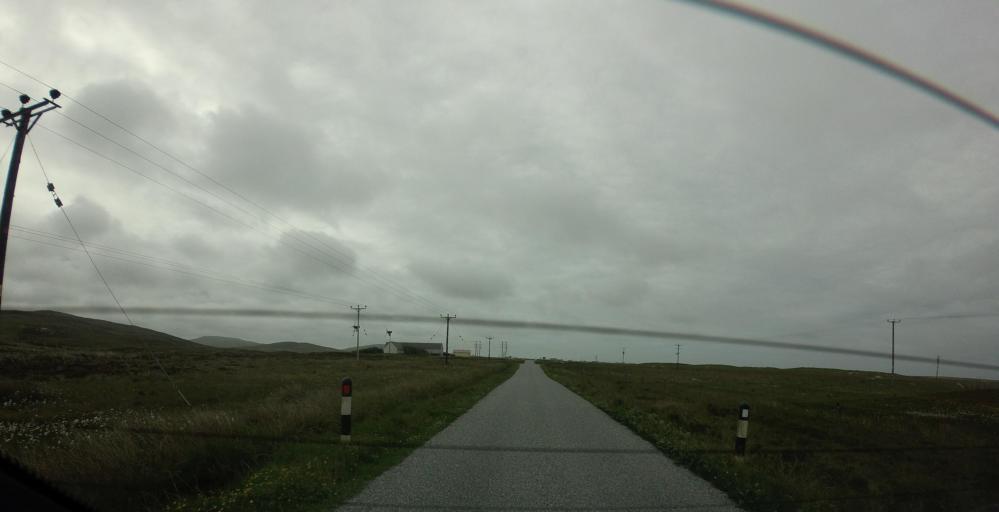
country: GB
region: Scotland
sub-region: Eilean Siar
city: Isle of South Uist
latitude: 57.2240
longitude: -7.3969
